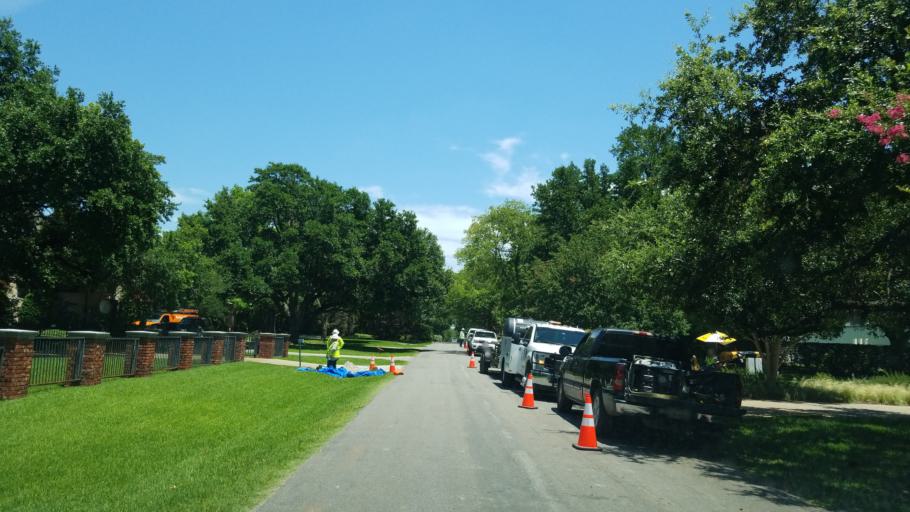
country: US
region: Texas
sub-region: Dallas County
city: University Park
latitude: 32.8755
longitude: -96.8363
